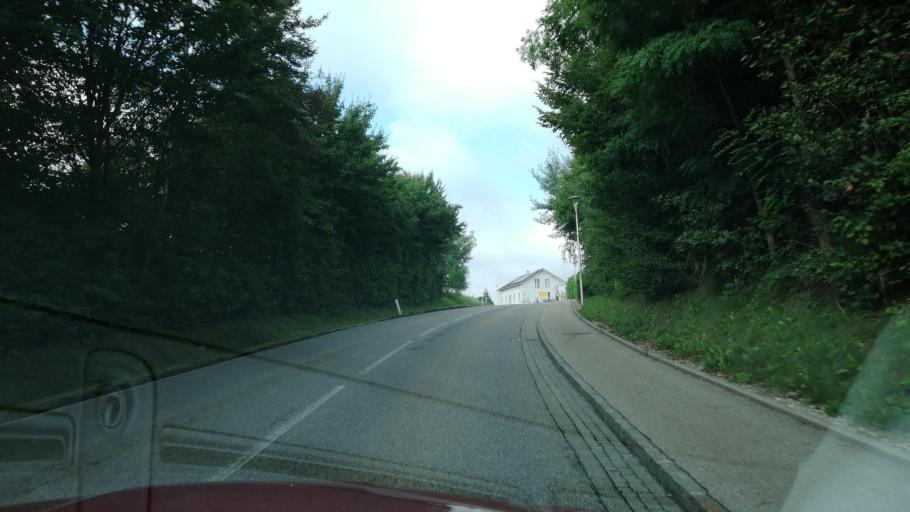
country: AT
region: Upper Austria
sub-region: Politischer Bezirk Braunau am Inn
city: Altheim
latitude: 48.2644
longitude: 13.3010
